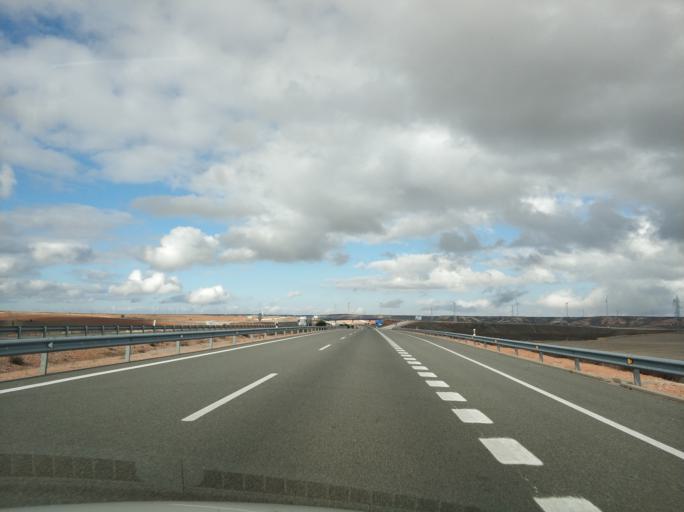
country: ES
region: Castille and Leon
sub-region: Provincia de Soria
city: Alcubilla de las Penas
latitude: 41.2556
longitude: -2.4735
